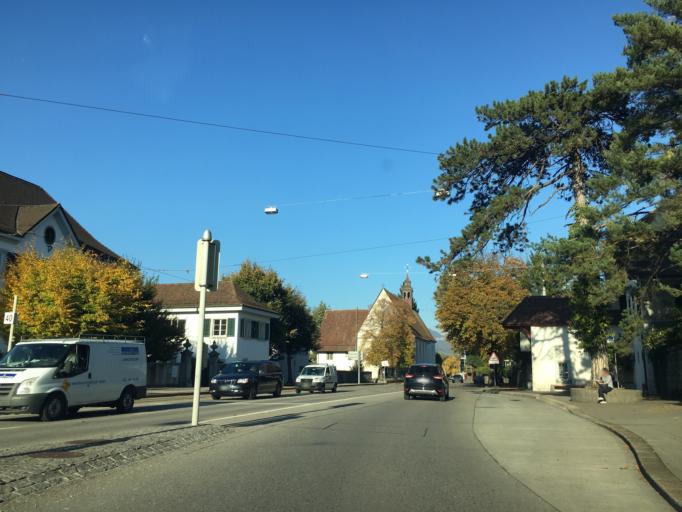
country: CH
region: Solothurn
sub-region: Bezirk Solothurn
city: Solothurn
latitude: 47.2096
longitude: 7.5415
